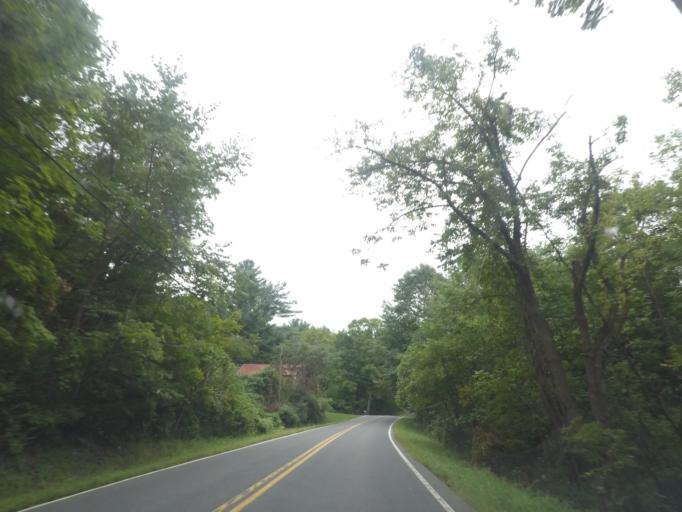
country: US
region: New York
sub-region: Rensselaer County
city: Nassau
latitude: 42.4832
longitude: -73.5938
